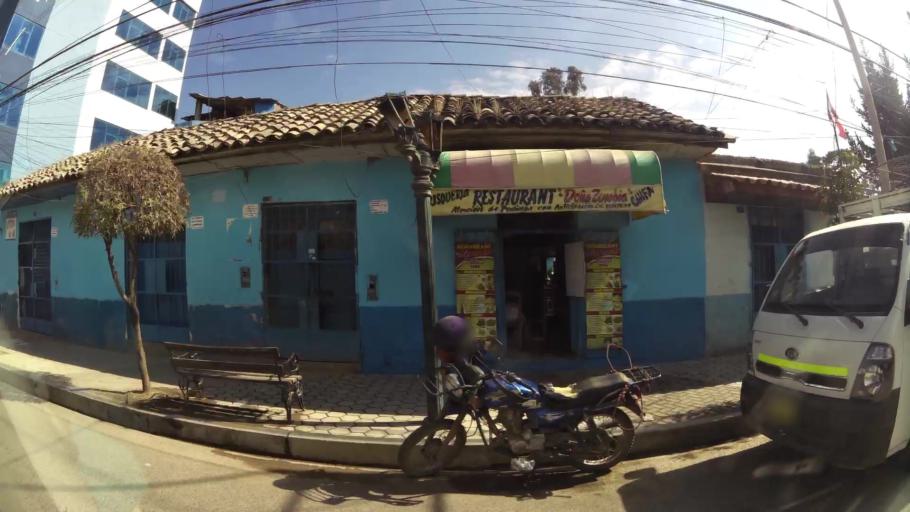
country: PE
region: Junin
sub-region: Provincia de Huancayo
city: Huancayo
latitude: -12.0633
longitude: -75.2004
